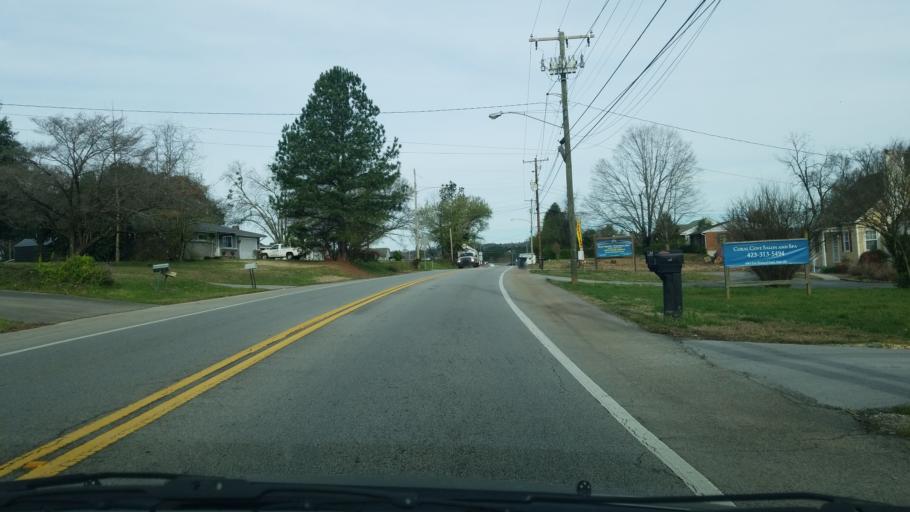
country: US
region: Tennessee
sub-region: Hamilton County
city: East Ridge
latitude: 35.0160
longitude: -85.2033
